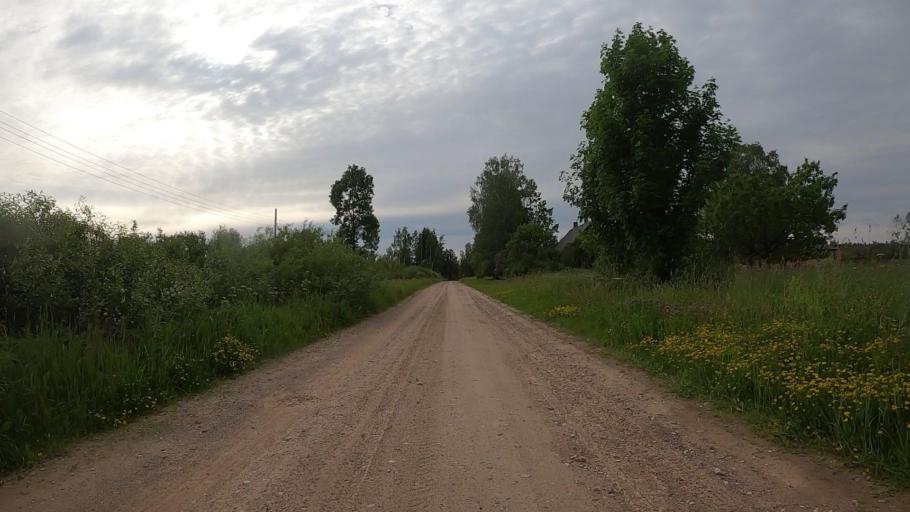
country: LV
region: Ozolnieku
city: Ozolnieki
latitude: 56.7147
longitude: 23.7901
